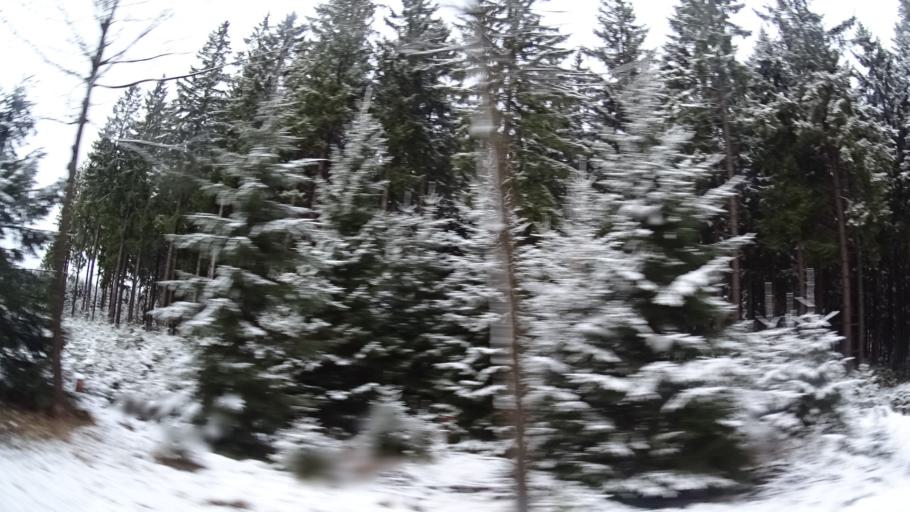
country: DE
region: Thuringia
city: Frankenhain
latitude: 50.7556
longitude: 10.7590
